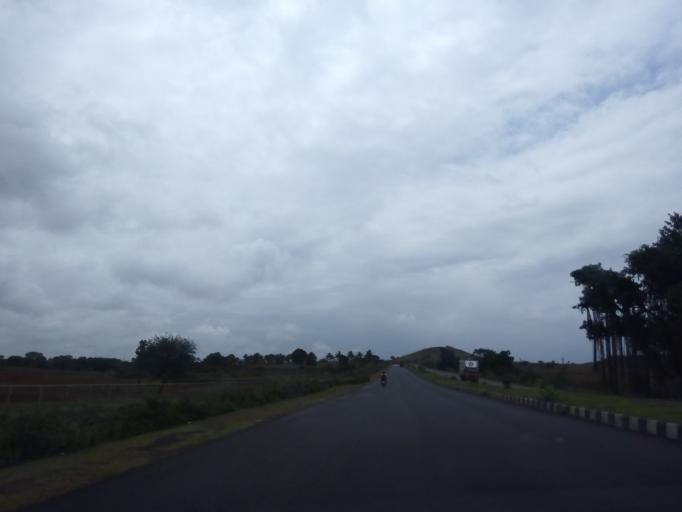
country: IN
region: Karnataka
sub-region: Haveri
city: Byadgi
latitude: 14.7163
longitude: 75.4941
